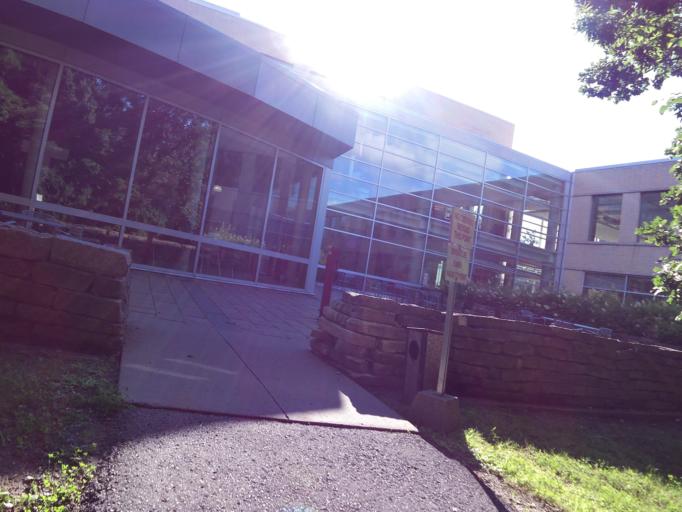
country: CA
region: Ontario
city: Bells Corners
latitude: 45.3520
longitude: -75.8538
